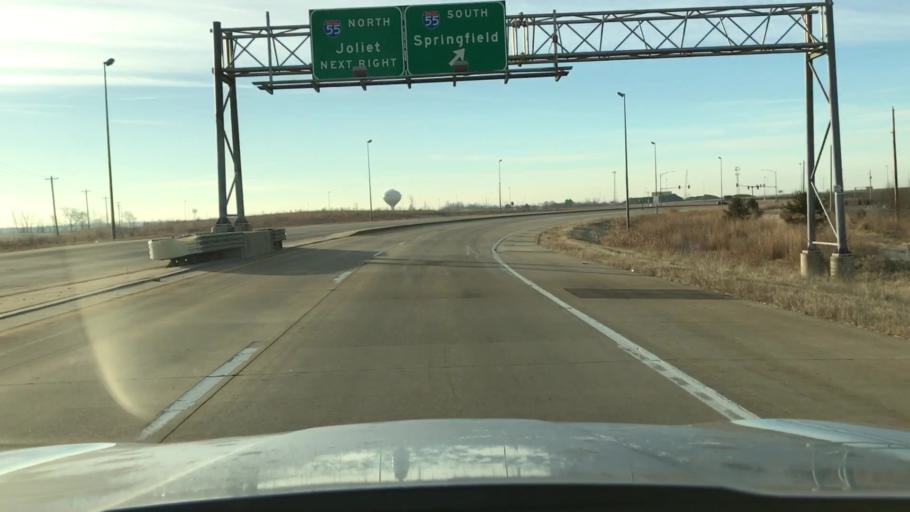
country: US
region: Illinois
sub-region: McLean County
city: Normal
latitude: 40.5434
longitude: -88.9443
